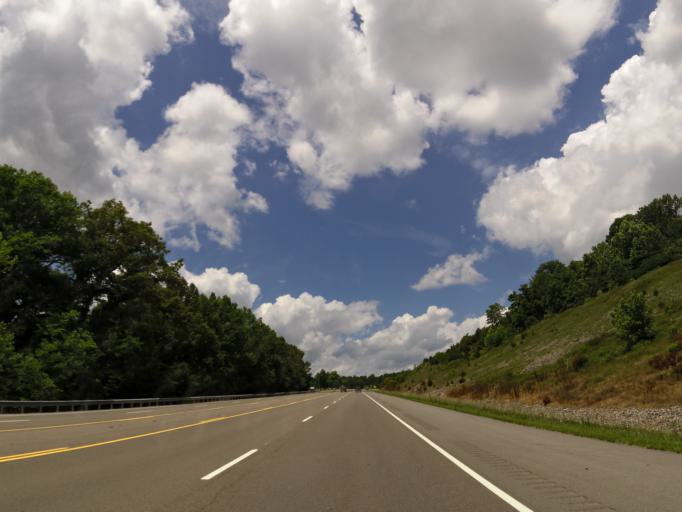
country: US
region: Tennessee
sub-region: Claiborne County
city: Harrogate
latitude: 36.5187
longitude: -83.6136
